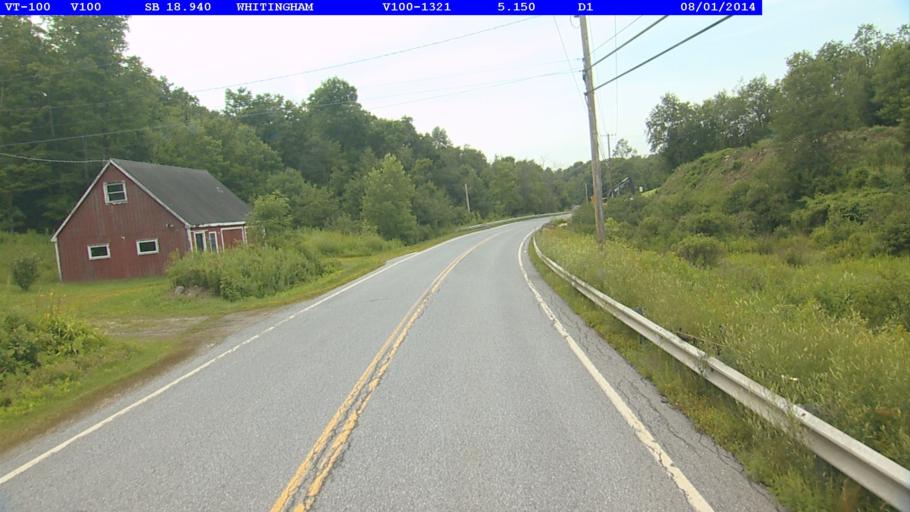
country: US
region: Massachusetts
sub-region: Franklin County
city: Charlemont
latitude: 42.7885
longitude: -72.8648
